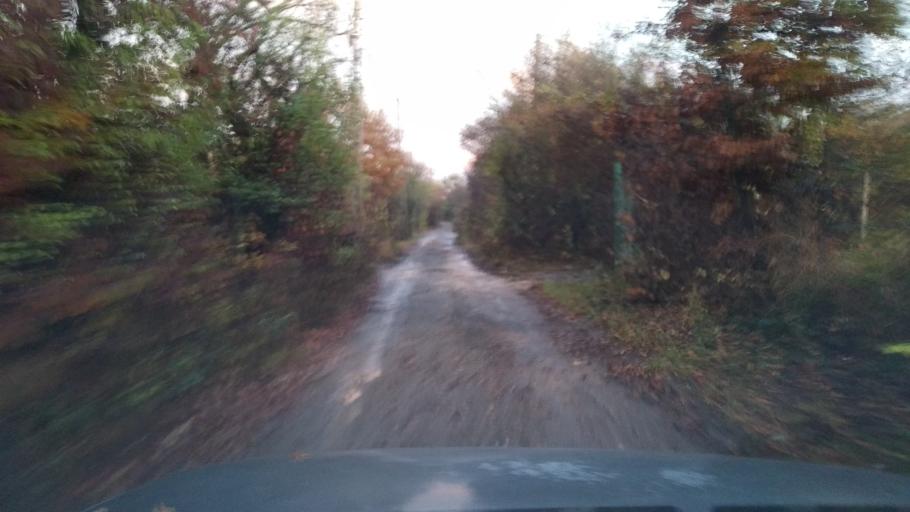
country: HU
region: Pest
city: Nagykovacsi
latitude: 47.6640
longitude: 19.0026
